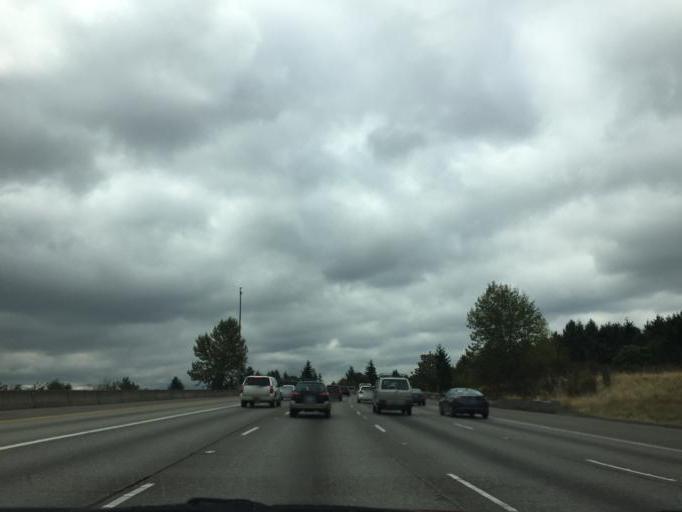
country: US
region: Washington
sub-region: King County
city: SeaTac
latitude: 47.4327
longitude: -122.2709
